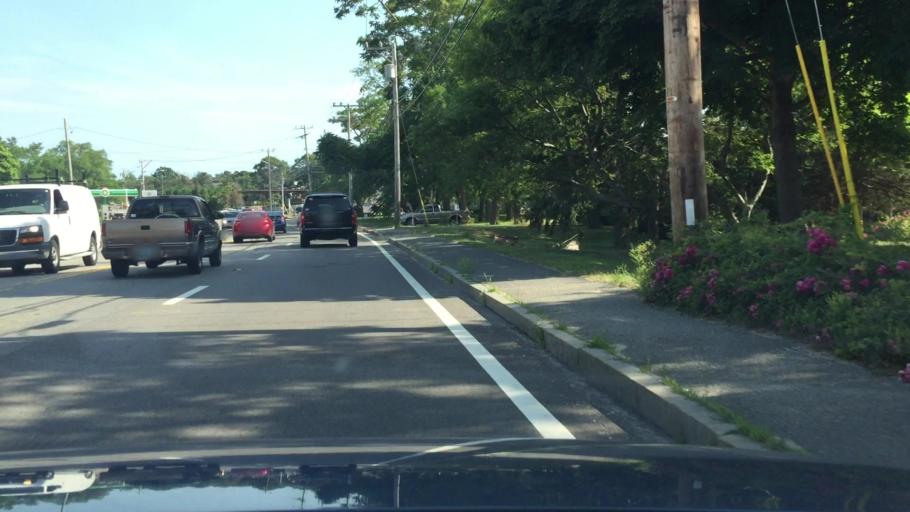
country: US
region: Massachusetts
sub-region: Barnstable County
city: Eastham
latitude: 41.8293
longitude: -69.9736
